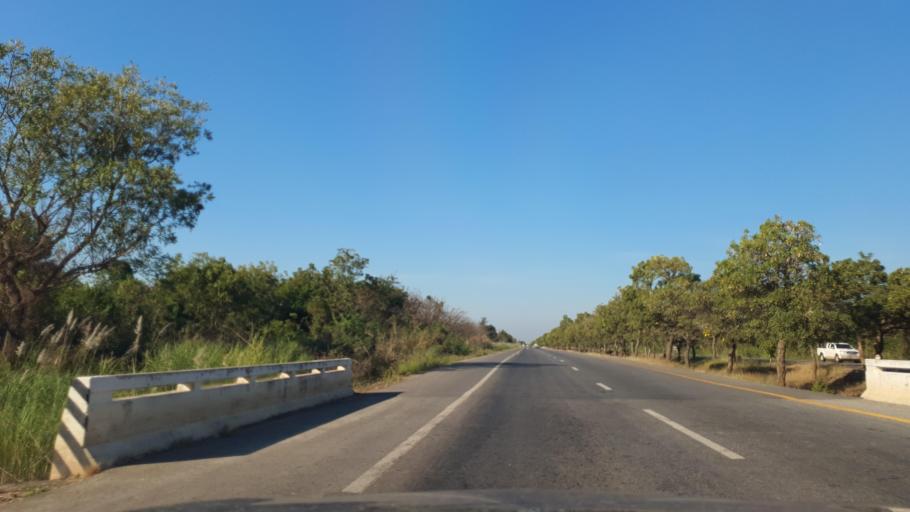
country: TH
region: Sukhothai
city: Sukhothai
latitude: 17.0703
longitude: 99.8043
